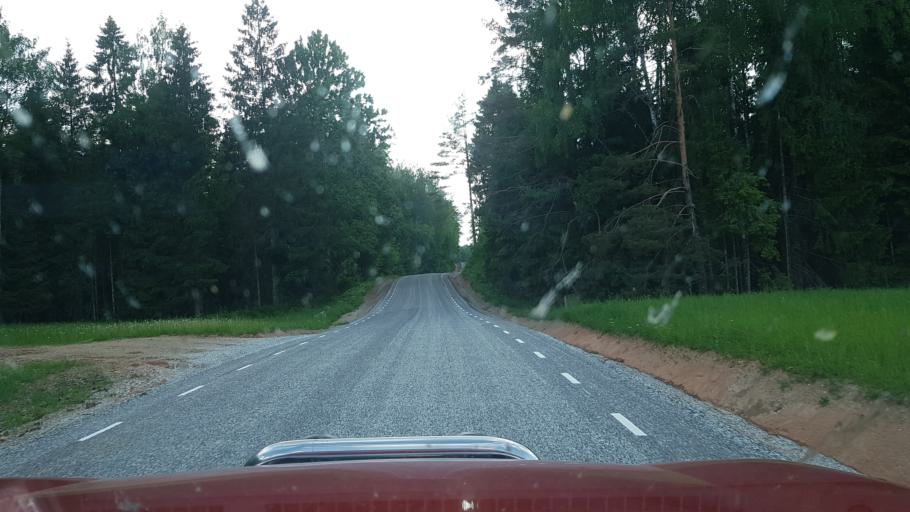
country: EE
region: Tartu
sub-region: UElenurme vald
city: Ulenurme
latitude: 58.1019
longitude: 26.7900
